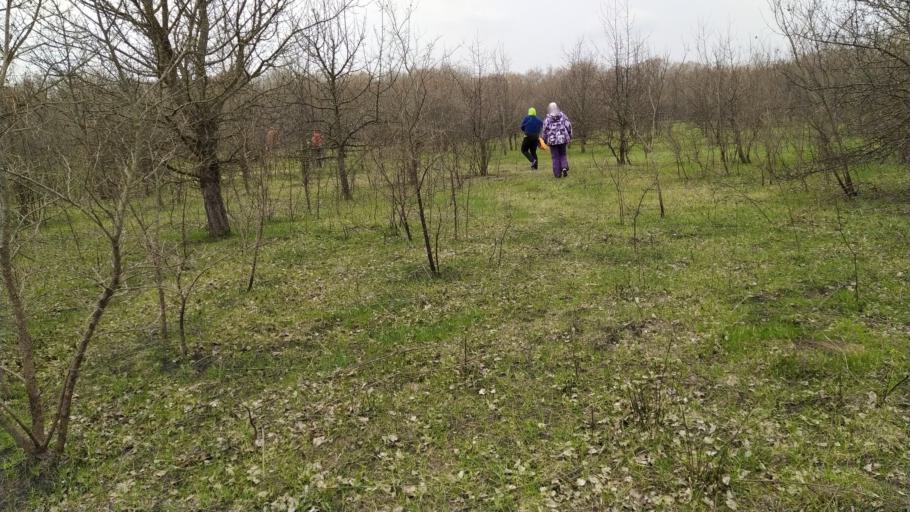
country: RU
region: Rostov
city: Semikarakorsk
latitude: 47.5401
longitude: 40.6814
